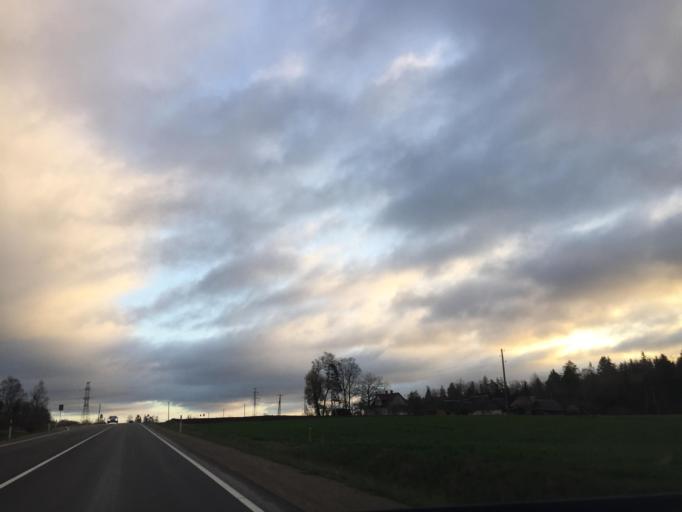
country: LV
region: Tukuma Rajons
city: Tukums
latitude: 56.9255
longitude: 23.0671
